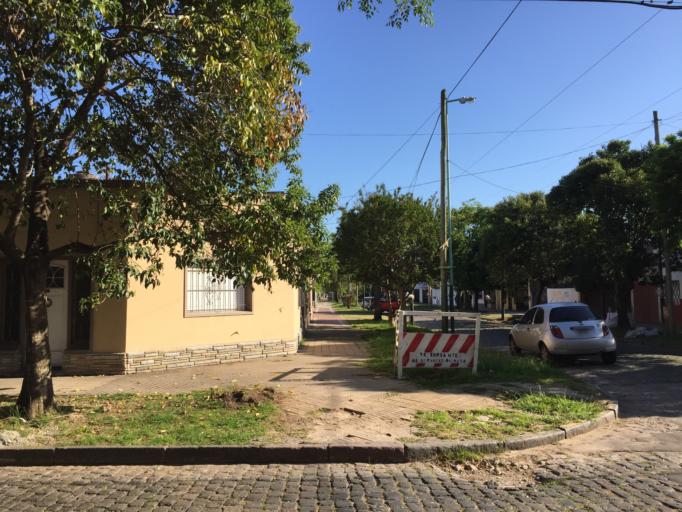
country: AR
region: Buenos Aires
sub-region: Partido de Lomas de Zamora
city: Lomas de Zamora
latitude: -34.7394
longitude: -58.3880
